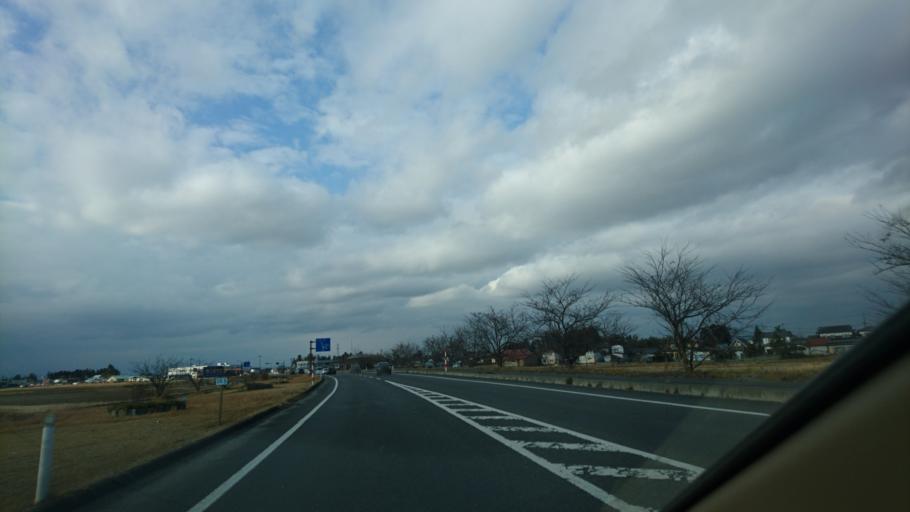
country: JP
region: Miyagi
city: Kogota
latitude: 38.5572
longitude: 141.0389
